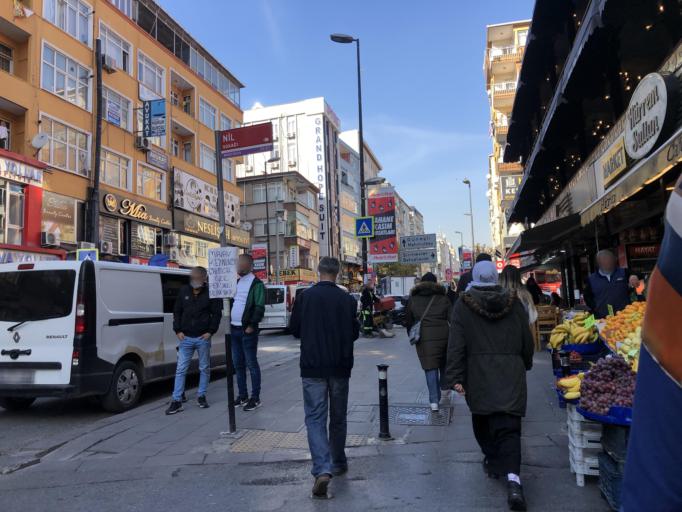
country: TR
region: Istanbul
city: Bahcelievler
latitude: 40.9936
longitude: 28.8433
